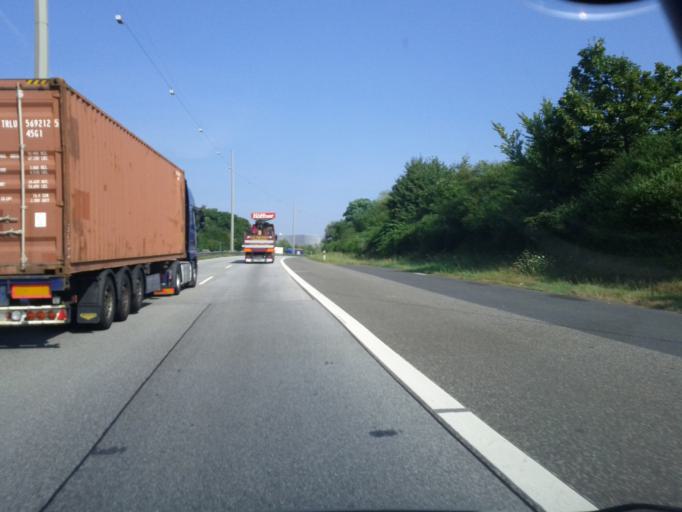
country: DE
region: Hamburg
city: Eidelstedt
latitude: 53.6147
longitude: 9.9139
